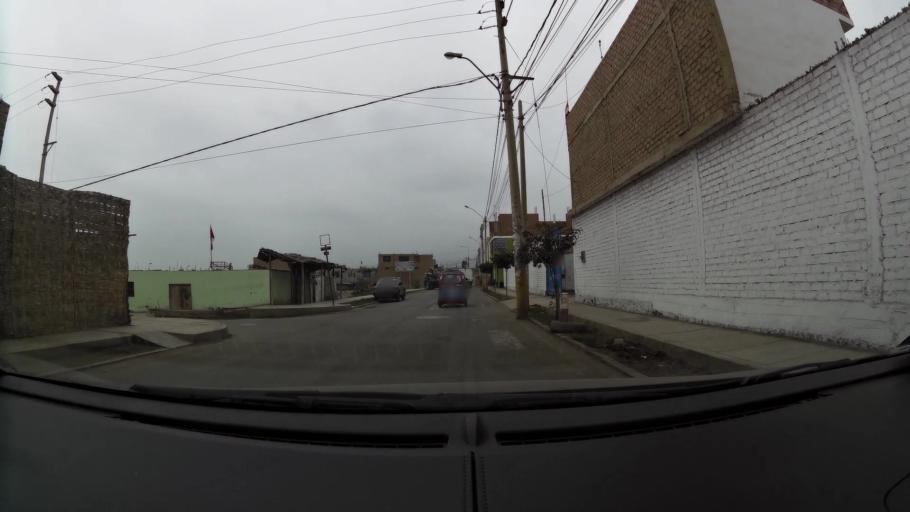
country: PE
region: Lima
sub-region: Barranca
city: Barranca
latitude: -10.7446
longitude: -77.7555
